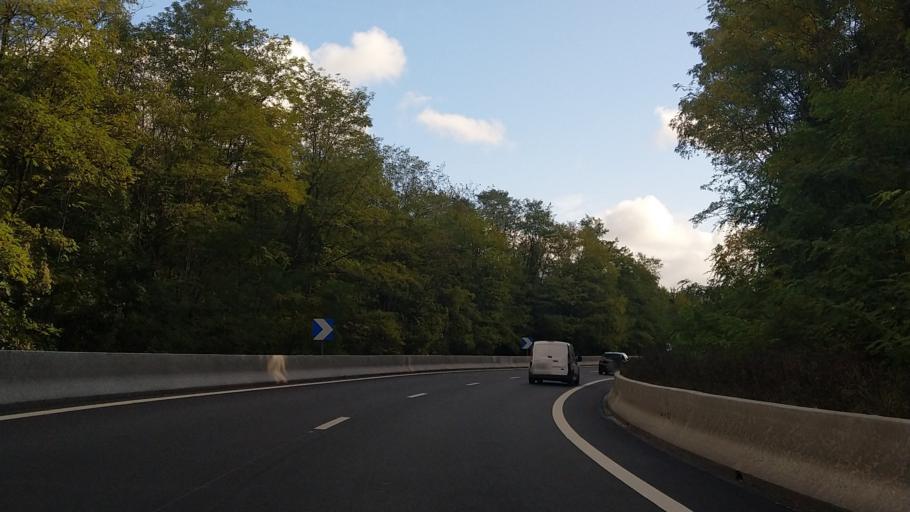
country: FR
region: Ile-de-France
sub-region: Departement du Val-d'Oise
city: Mours
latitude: 49.1029
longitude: 2.2655
